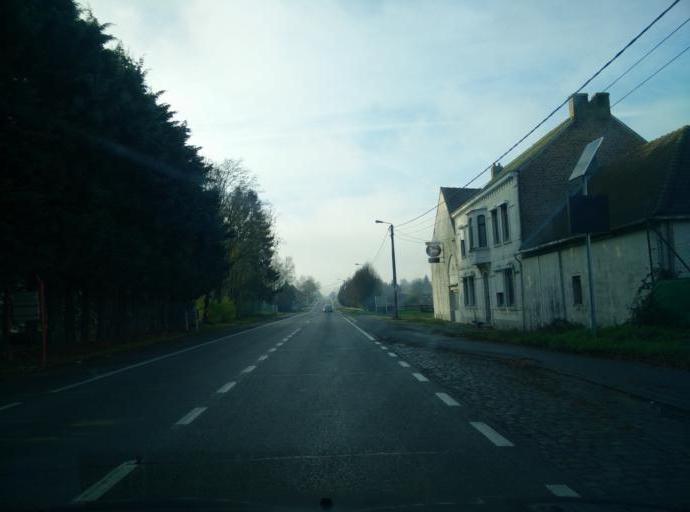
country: BE
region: Wallonia
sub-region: Province du Brabant Wallon
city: Rebecq-Rognon
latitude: 50.6916
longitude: 4.1028
